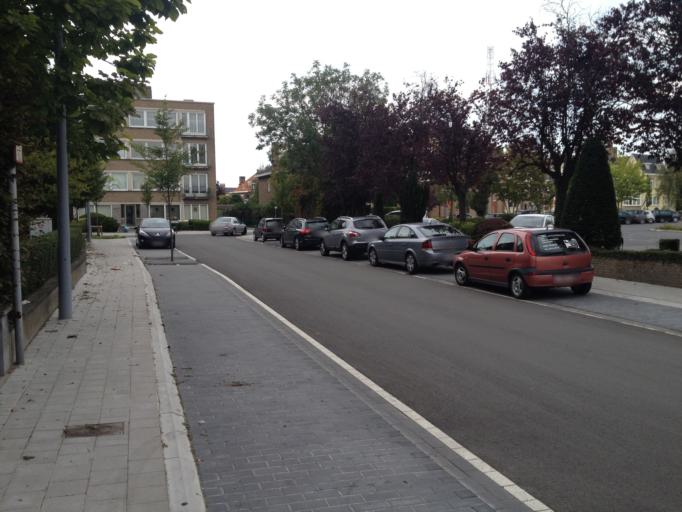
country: BE
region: Flanders
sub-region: Provincie West-Vlaanderen
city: Brugge
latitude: 51.2161
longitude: 3.2122
